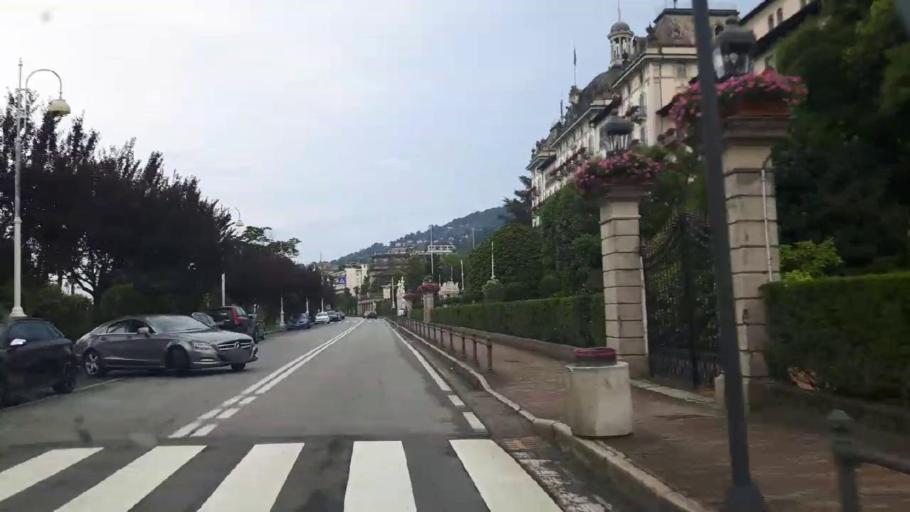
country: IT
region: Piedmont
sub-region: Provincia Verbano-Cusio-Ossola
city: Stresa
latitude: 45.8875
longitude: 8.5324
